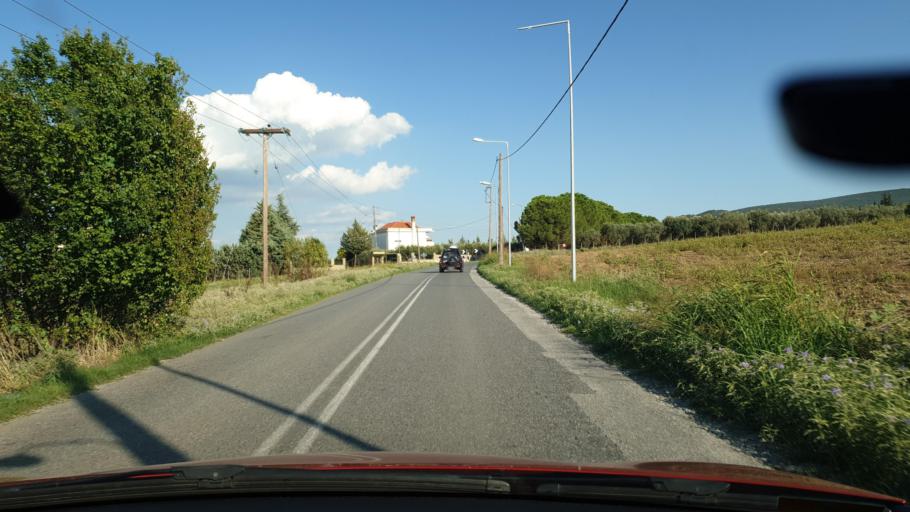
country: GR
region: Central Macedonia
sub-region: Nomos Thessalonikis
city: Agia Paraskevi
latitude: 40.4886
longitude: 23.0382
